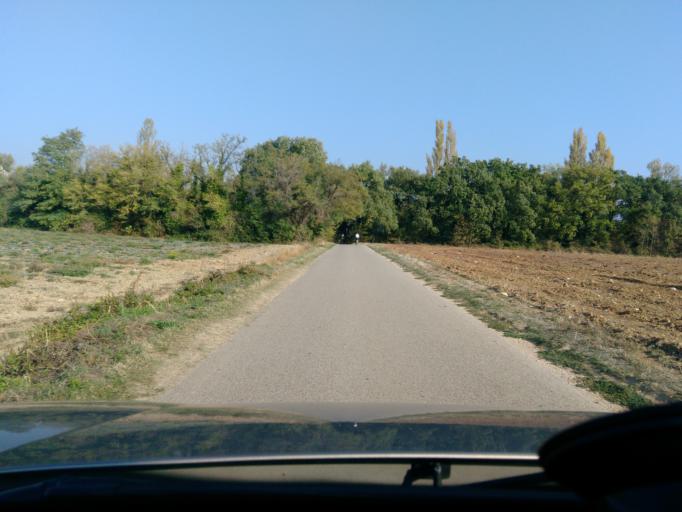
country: FR
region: Rhone-Alpes
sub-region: Departement de la Drome
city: Montboucher-sur-Jabron
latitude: 44.5416
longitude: 4.8085
